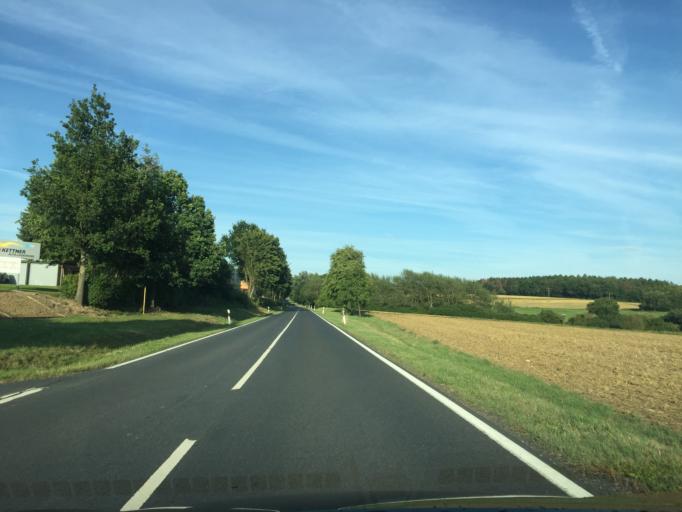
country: DE
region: Rheinland-Pfalz
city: Heiligenroth
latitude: 50.4587
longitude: 7.8739
